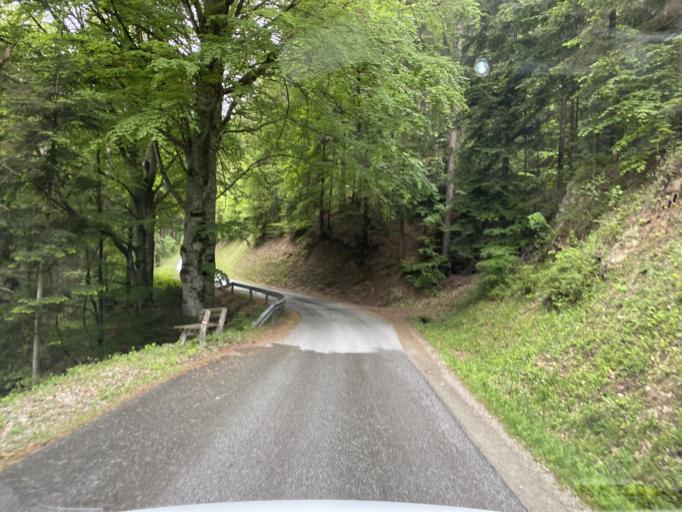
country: AT
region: Styria
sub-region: Politischer Bezirk Weiz
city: Koglhof
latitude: 47.3324
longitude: 15.6725
